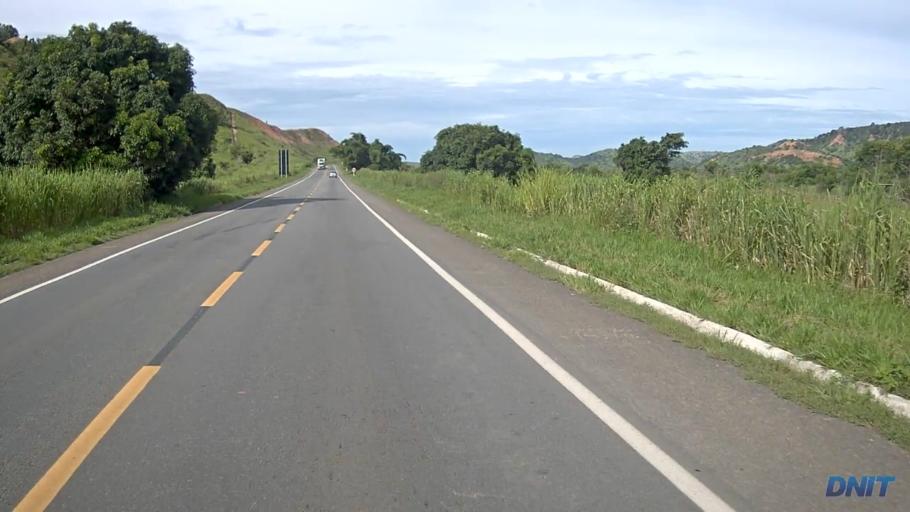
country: BR
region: Minas Gerais
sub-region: Belo Oriente
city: Belo Oriente
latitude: -19.1799
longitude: -42.2594
